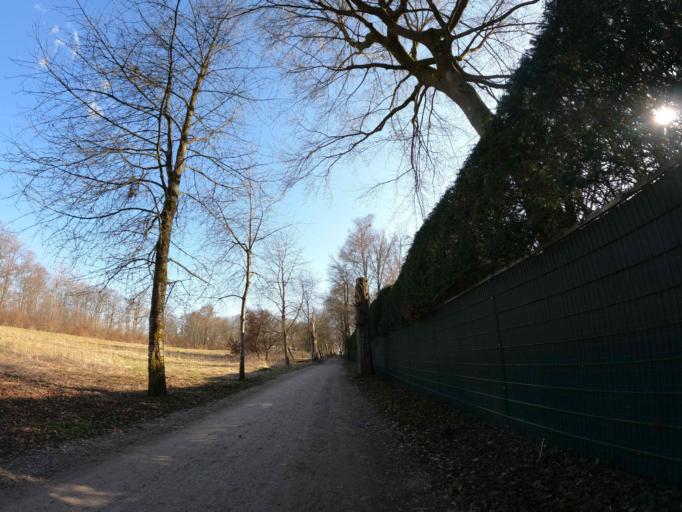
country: DE
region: Bavaria
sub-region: Upper Bavaria
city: Pullach im Isartal
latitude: 48.0697
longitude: 11.5385
